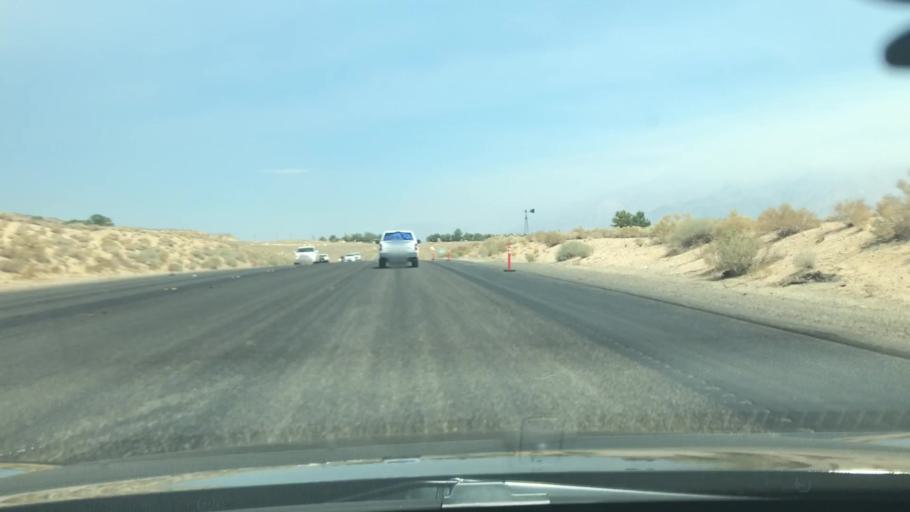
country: US
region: California
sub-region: Inyo County
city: Lone Pine
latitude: 36.5326
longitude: -118.0454
